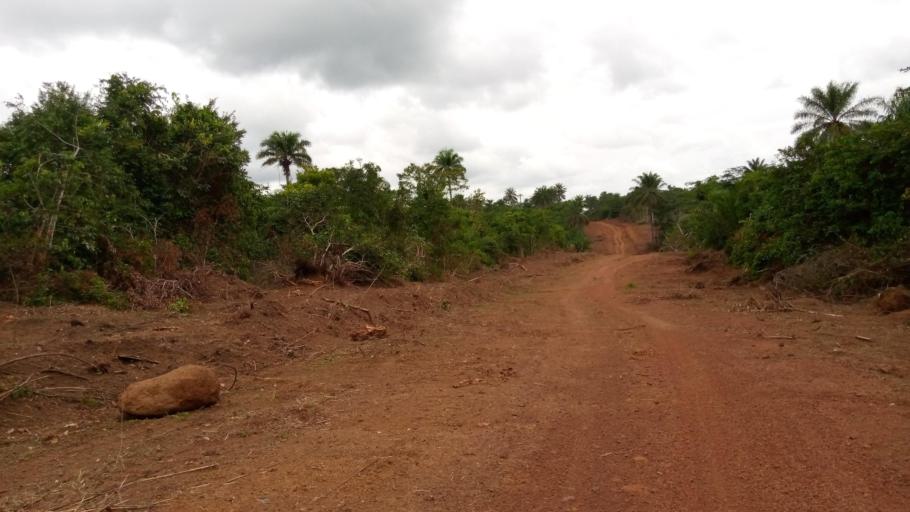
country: SL
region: Southern Province
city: Moyamba
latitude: 8.1946
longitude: -12.5371
